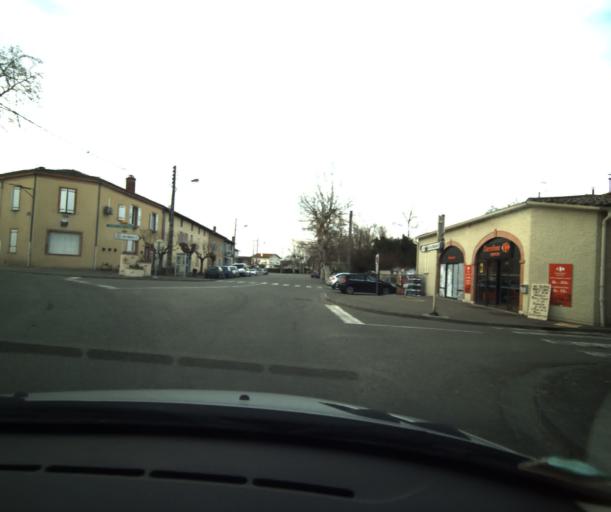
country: FR
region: Midi-Pyrenees
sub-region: Departement du Tarn-et-Garonne
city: Montech
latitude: 43.9564
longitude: 1.2280
